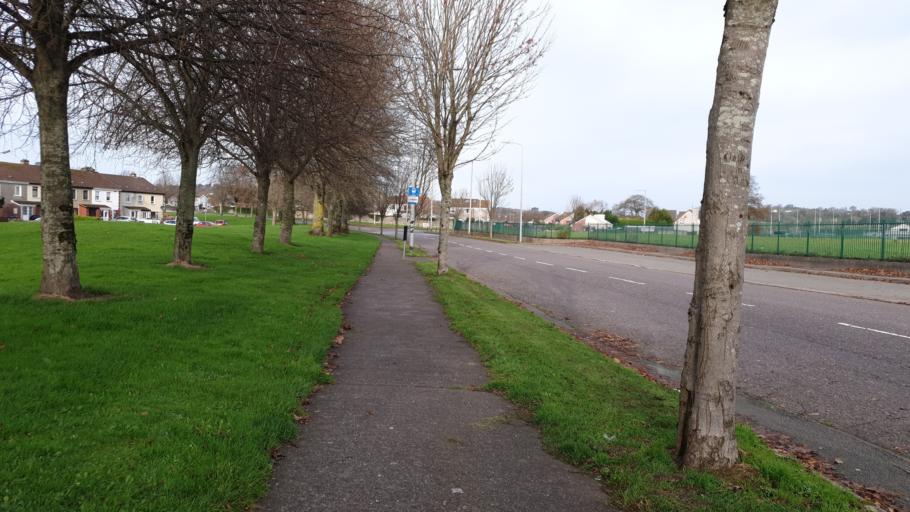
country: IE
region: Munster
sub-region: County Cork
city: Passage West
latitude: 51.8935
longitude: -8.3963
